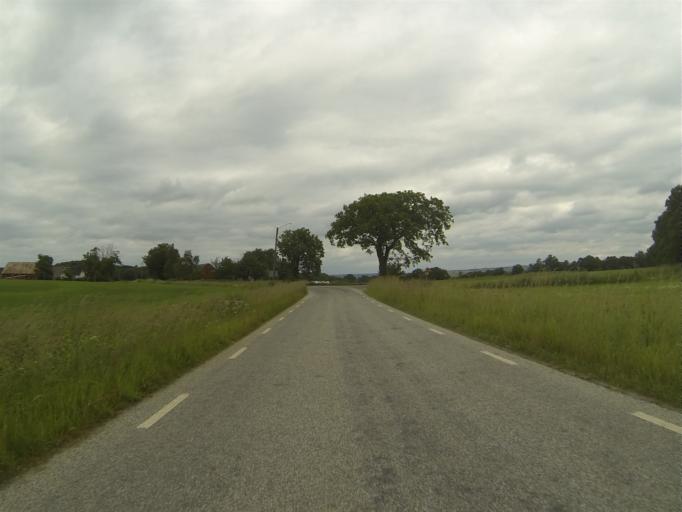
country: SE
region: Skane
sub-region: Lunds Kommun
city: Lund
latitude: 55.7251
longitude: 13.3042
